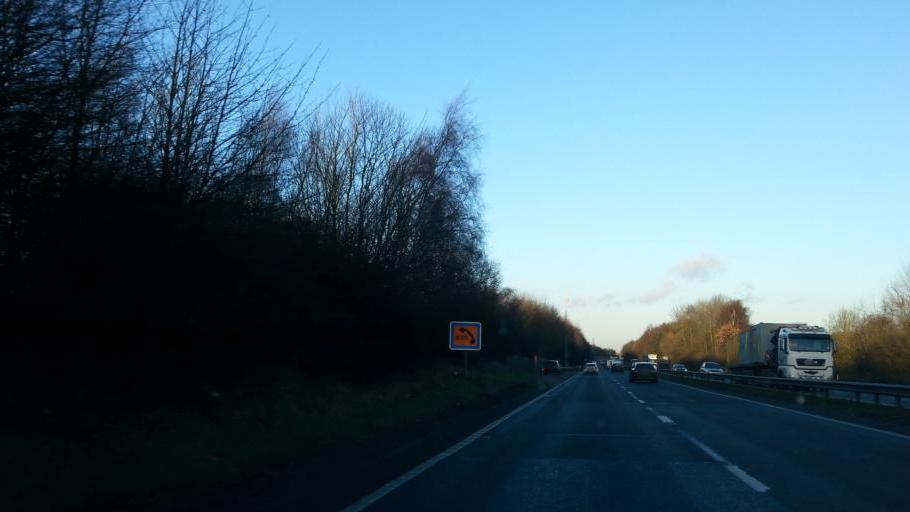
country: GB
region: England
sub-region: Derbyshire
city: Melbourne
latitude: 52.7761
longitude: -1.4206
